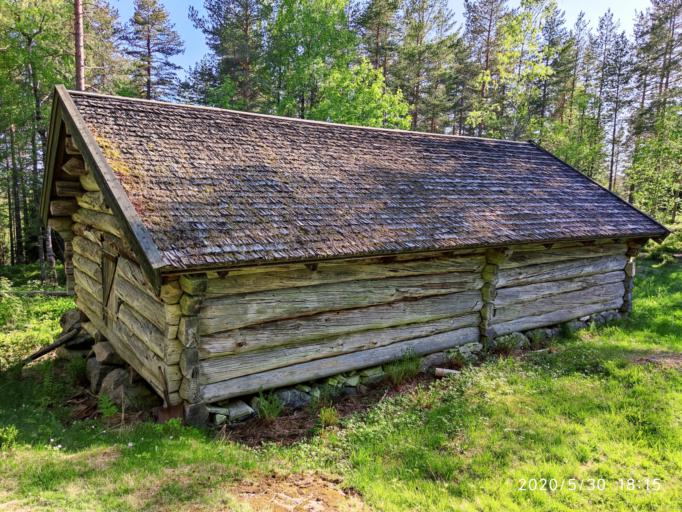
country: NO
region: Buskerud
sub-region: Drammen
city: Drammen
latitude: 59.7574
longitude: 10.2009
